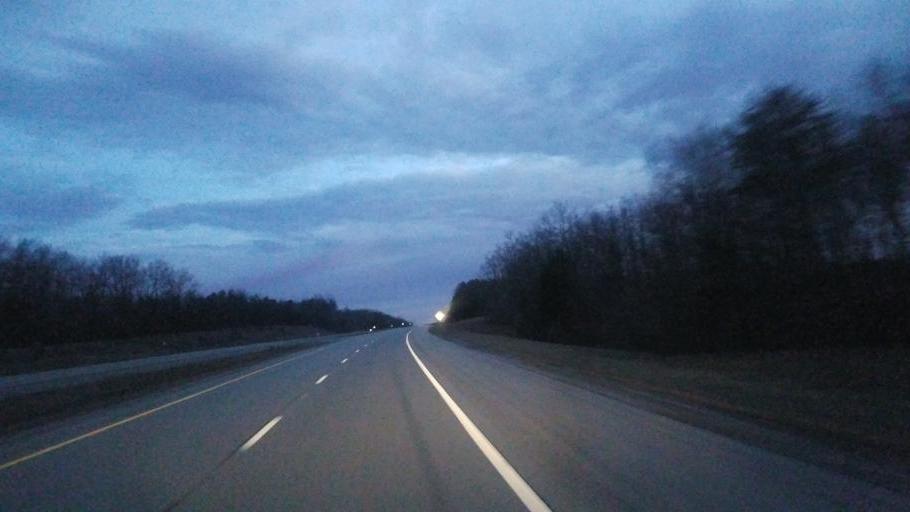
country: US
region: Tennessee
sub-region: Van Buren County
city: Spencer
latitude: 35.5824
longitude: -85.4713
